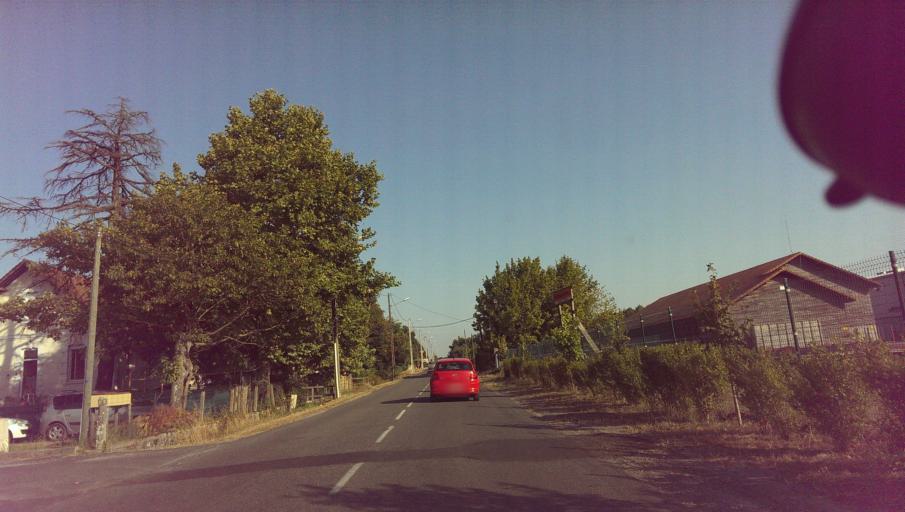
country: FR
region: Aquitaine
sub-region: Departement des Landes
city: Mimizan
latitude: 44.1960
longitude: -1.2224
